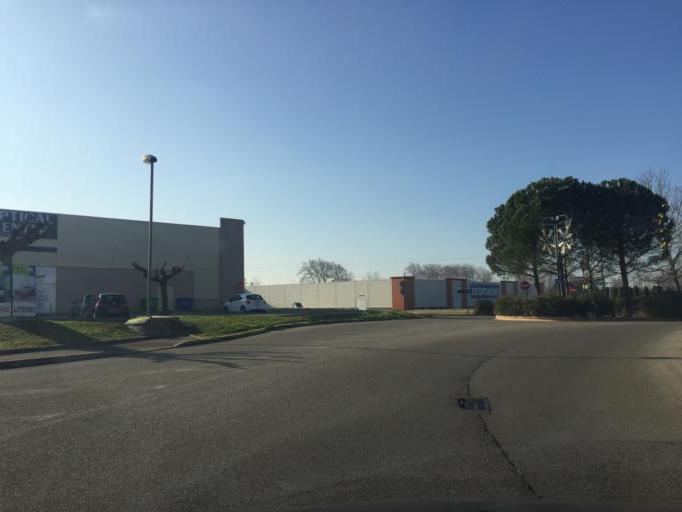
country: FR
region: Provence-Alpes-Cote d'Azur
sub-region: Departement du Vaucluse
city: Montfavet
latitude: 43.9198
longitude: 4.8695
